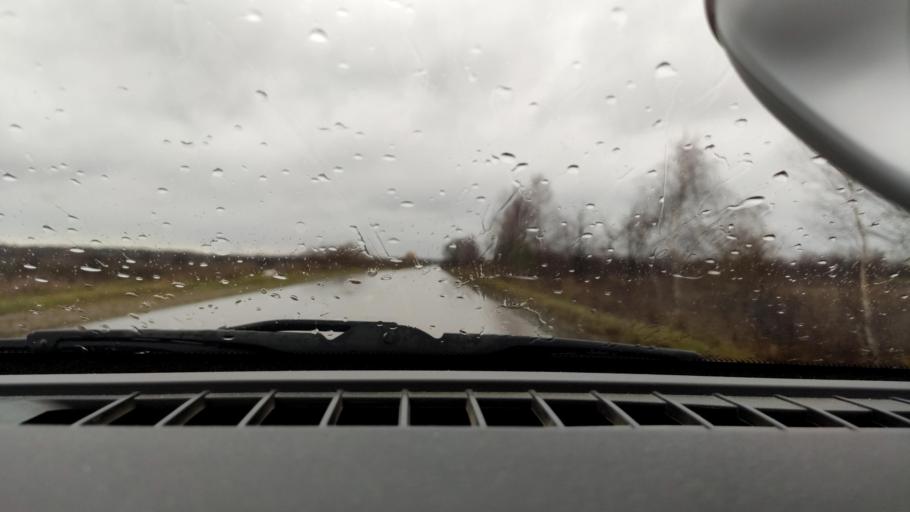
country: RU
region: Perm
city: Kondratovo
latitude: 57.9979
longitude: 56.0799
